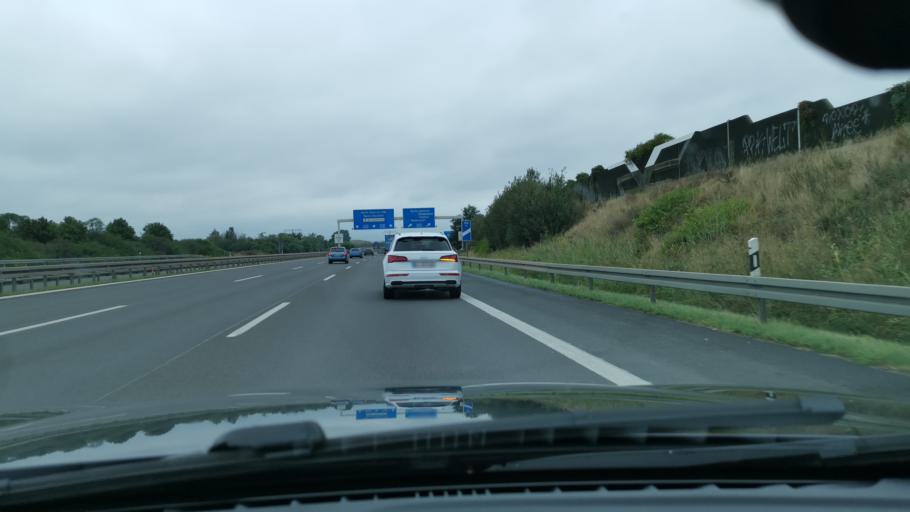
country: DE
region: Brandenburg
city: Schulzendorf
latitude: 52.3575
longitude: 13.5496
